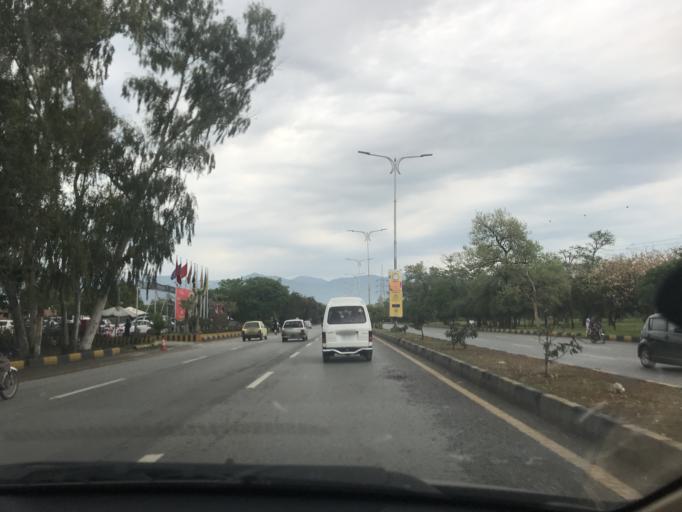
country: PK
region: Islamabad
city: Islamabad
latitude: 33.6930
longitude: 73.1102
